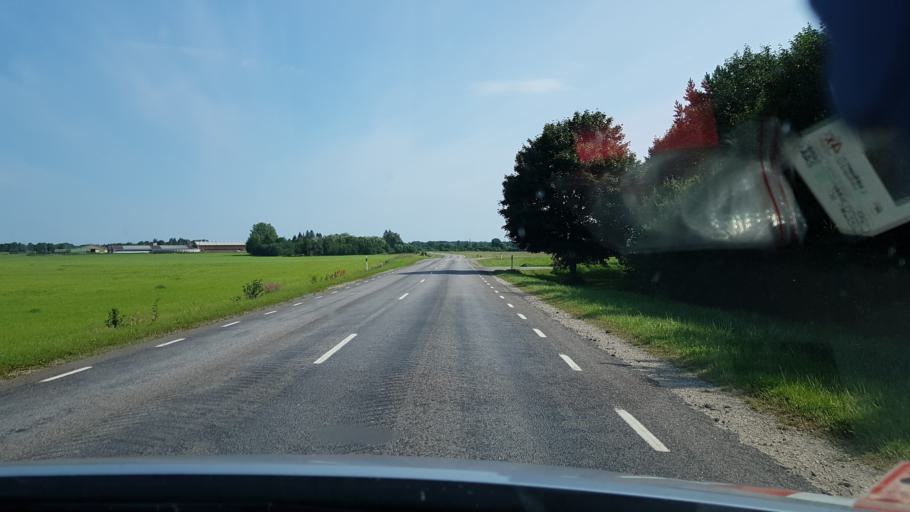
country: EE
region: Harju
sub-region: Nissi vald
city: Turba
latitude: 58.9088
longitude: 24.1334
